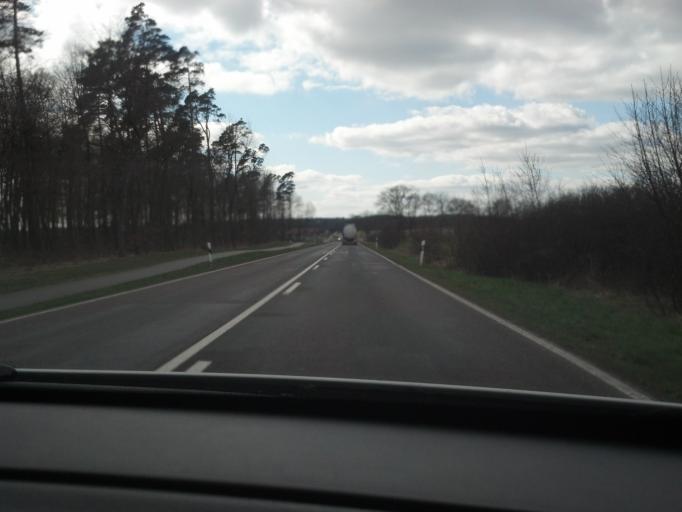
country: DE
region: Mecklenburg-Vorpommern
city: Malchow
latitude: 53.3646
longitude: 12.4446
